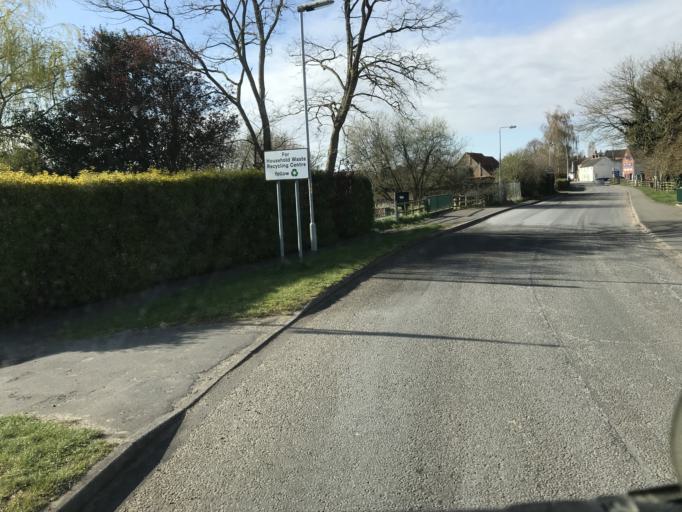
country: GB
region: England
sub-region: Lincolnshire
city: Market Rasen
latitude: 53.3890
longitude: -0.3313
